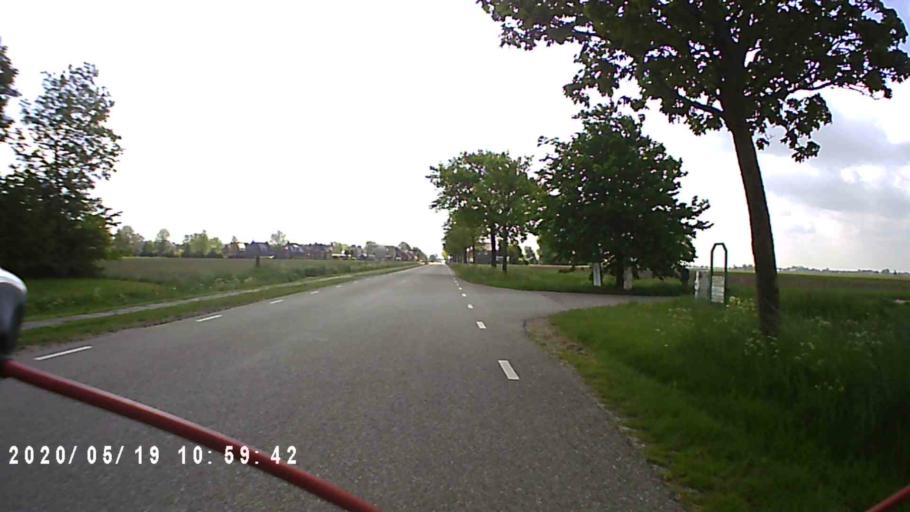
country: NL
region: Groningen
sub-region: Gemeente Zuidhorn
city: Grijpskerk
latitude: 53.3061
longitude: 6.2654
